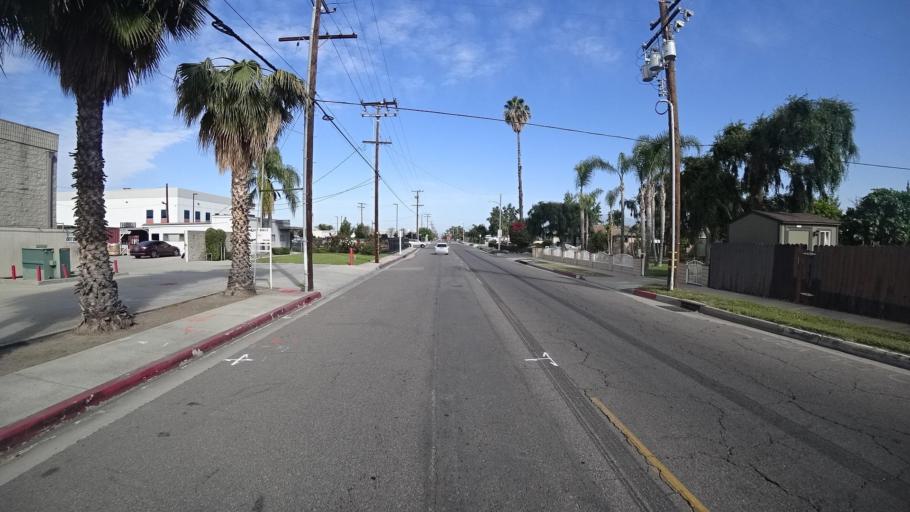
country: US
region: California
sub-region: Los Angeles County
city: La Puente
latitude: 34.0318
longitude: -117.9652
